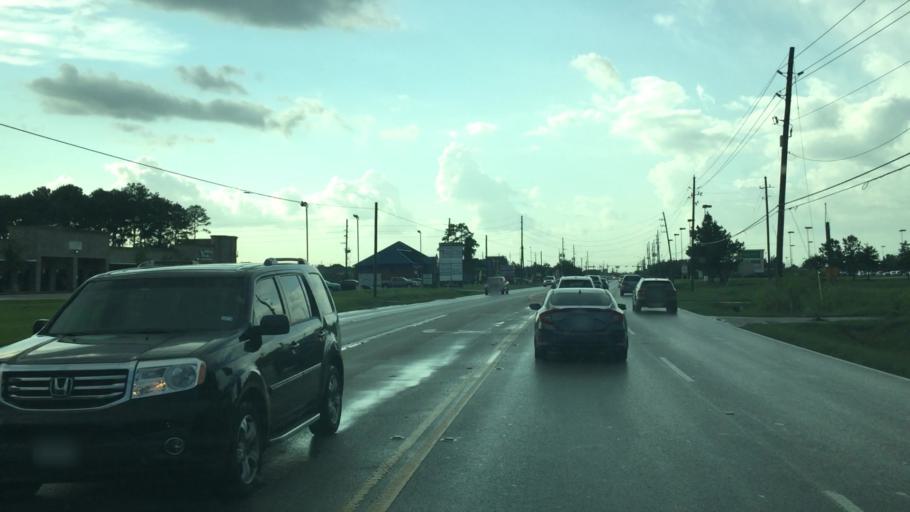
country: US
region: Texas
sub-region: Harris County
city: Spring
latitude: 30.0678
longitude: -95.5066
